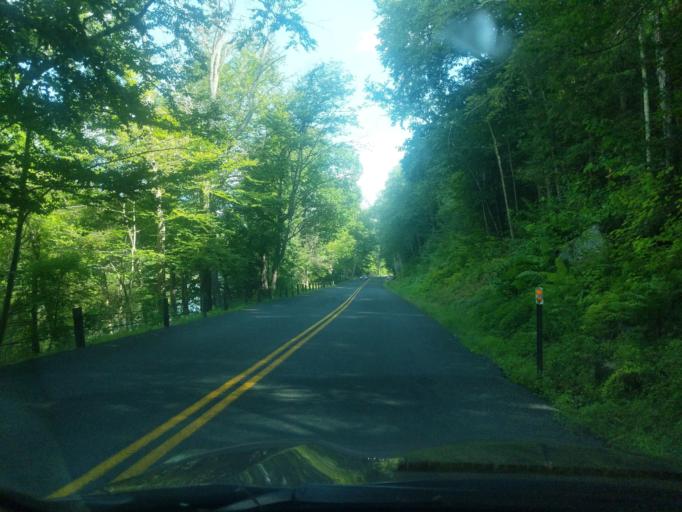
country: US
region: Connecticut
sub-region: Litchfield County
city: New Hartford Center
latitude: 41.9204
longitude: -72.9961
